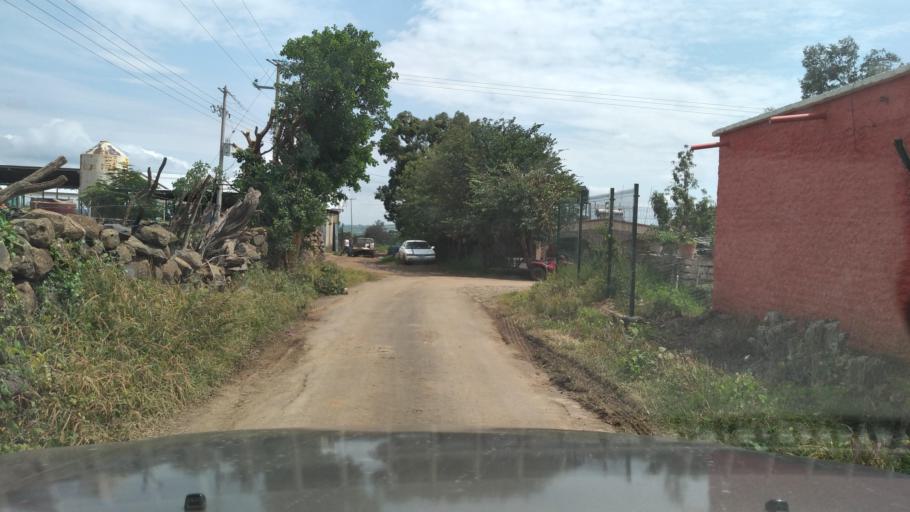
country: MX
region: Jalisco
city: Capilla de Guadalupe
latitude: 20.7491
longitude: -102.6326
